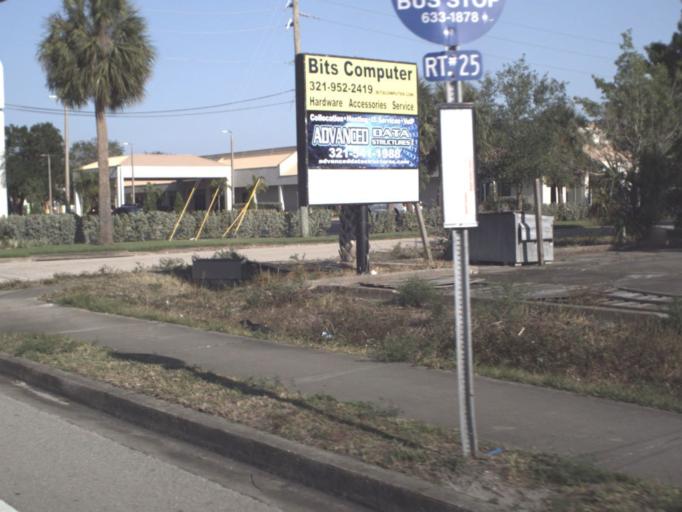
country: US
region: Florida
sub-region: Brevard County
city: West Melbourne
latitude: 28.0787
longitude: -80.6406
